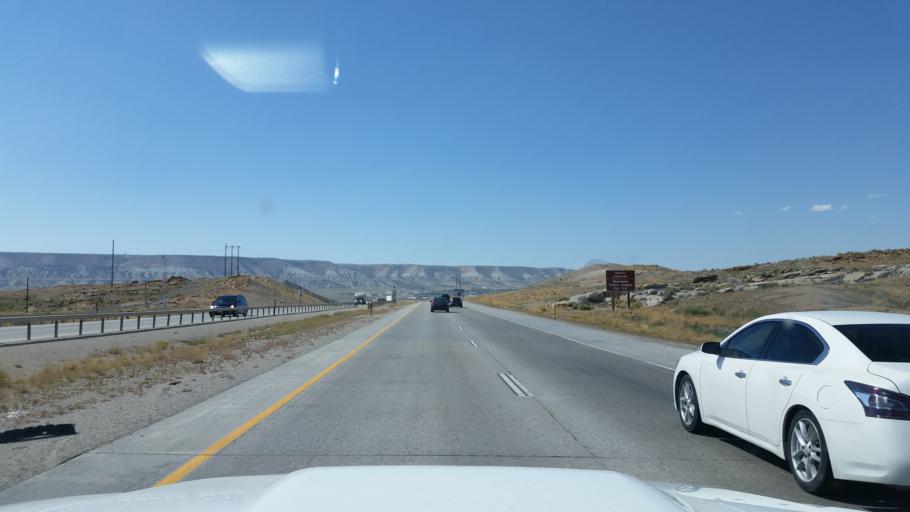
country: US
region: Wyoming
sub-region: Sweetwater County
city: Rock Springs
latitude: 41.6077
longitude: -109.2113
